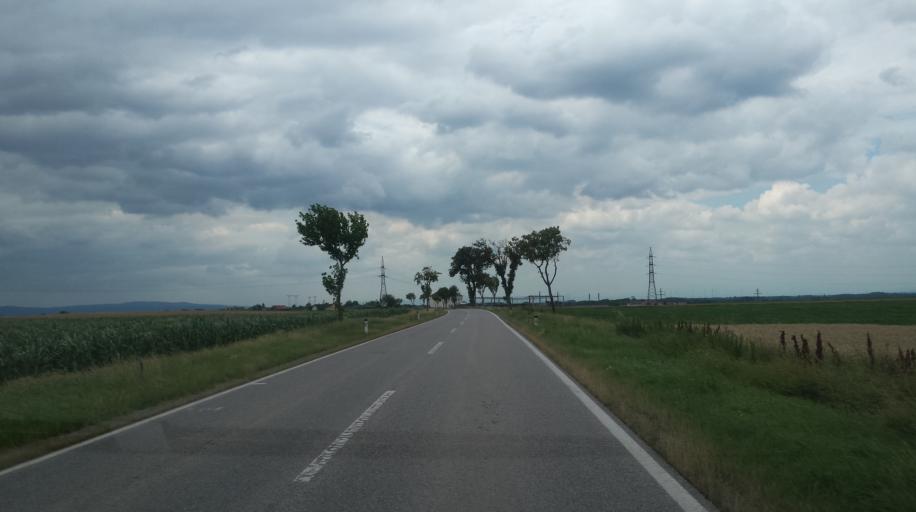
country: AT
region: Lower Austria
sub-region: Politischer Bezirk Wien-Umgebung
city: Moosbrunn
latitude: 48.0320
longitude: 16.4654
